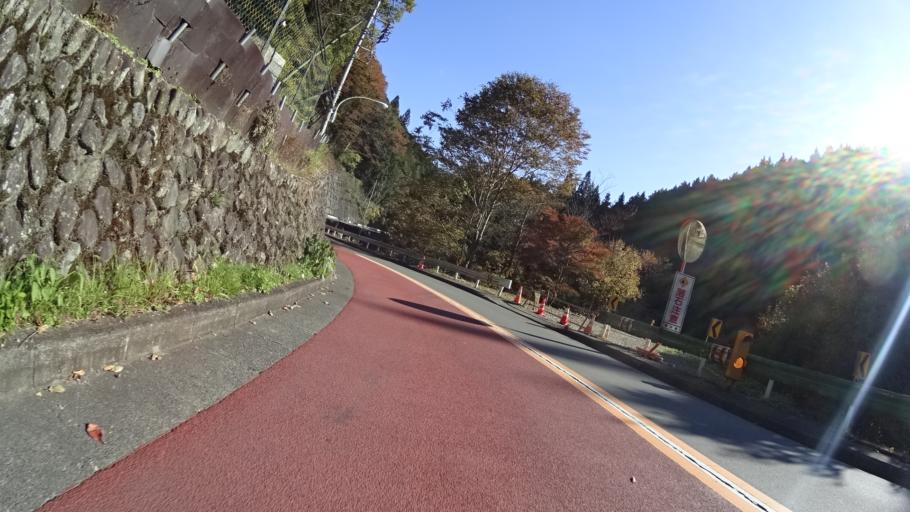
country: JP
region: Yamanashi
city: Uenohara
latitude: 35.7102
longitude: 139.0931
